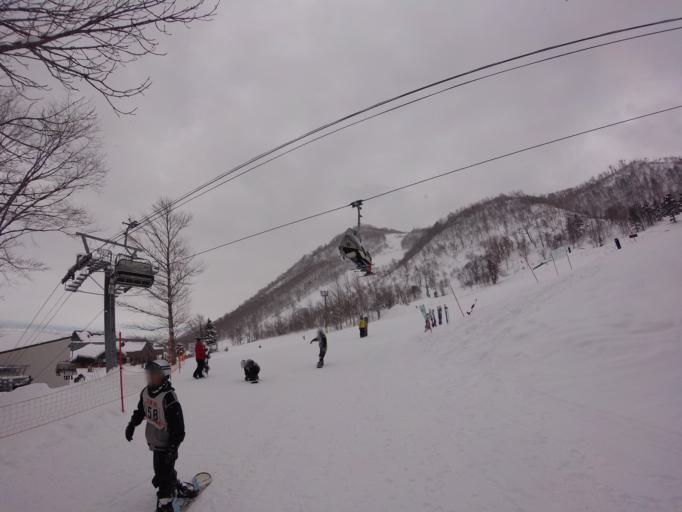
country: JP
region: Hokkaido
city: Sapporo
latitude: 43.0835
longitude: 141.2037
